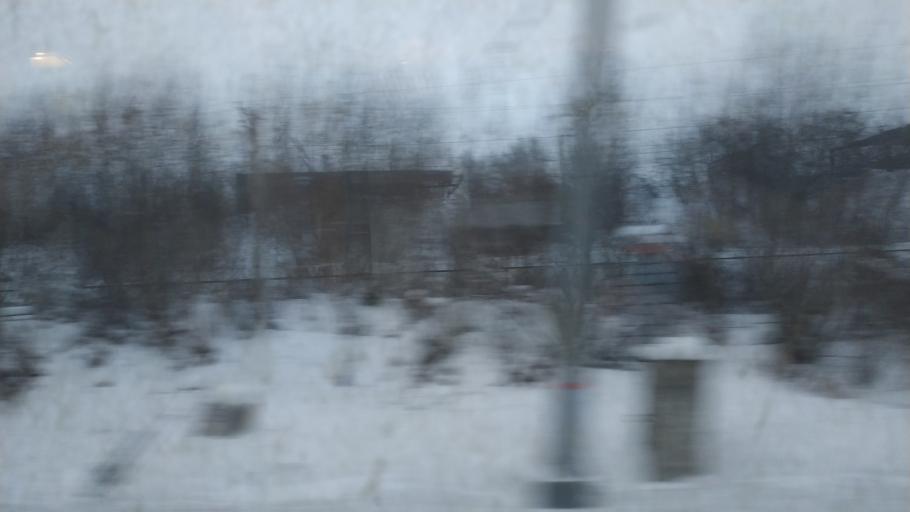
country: RU
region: Moskovskaya
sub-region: Podol'skiy Rayon
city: Podol'sk
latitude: 55.4596
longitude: 37.5627
